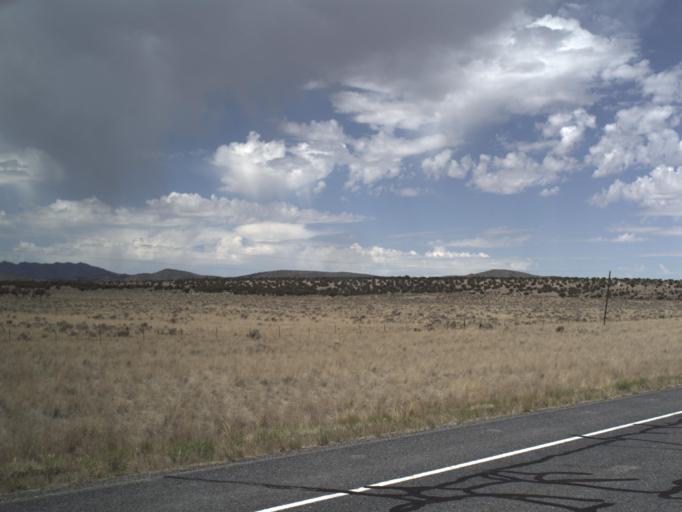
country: US
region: Utah
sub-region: Utah County
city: Eagle Mountain
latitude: 40.0598
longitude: -112.3108
